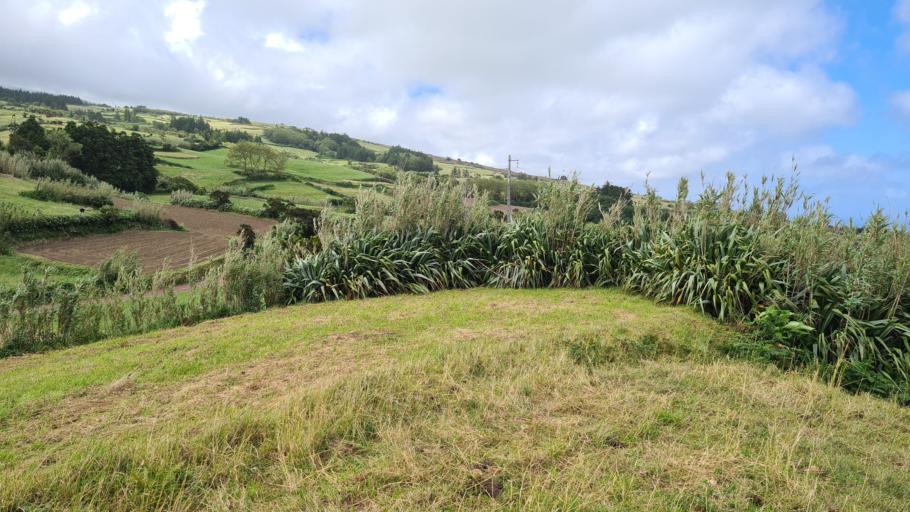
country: PT
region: Azores
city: Ribeira Grande
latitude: 38.6260
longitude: -28.7121
